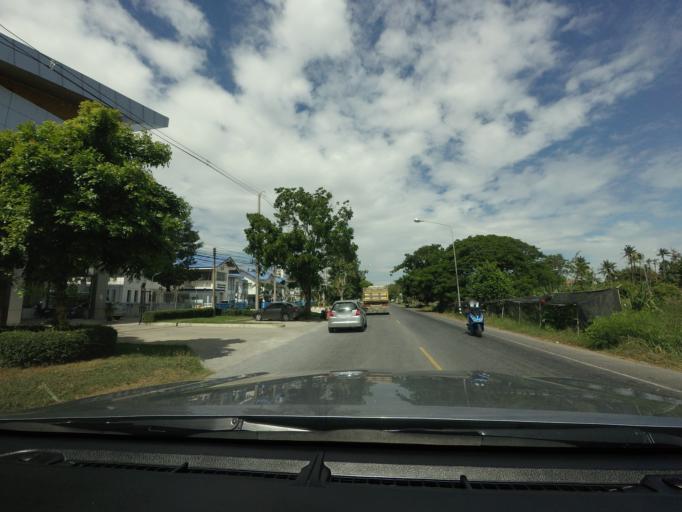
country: TH
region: Suphan Buri
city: Suphan Buri
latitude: 14.4706
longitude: 100.0914
